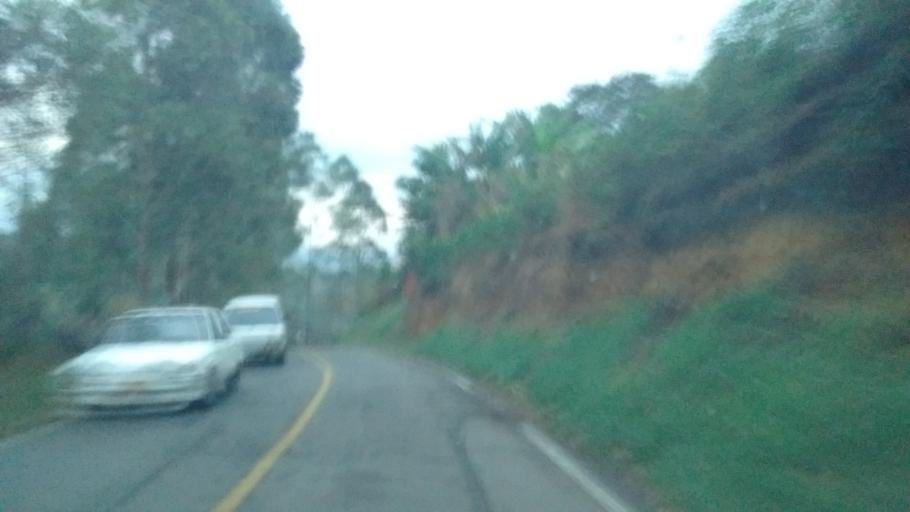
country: CO
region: Cauca
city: Popayan
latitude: 2.3664
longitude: -76.6870
